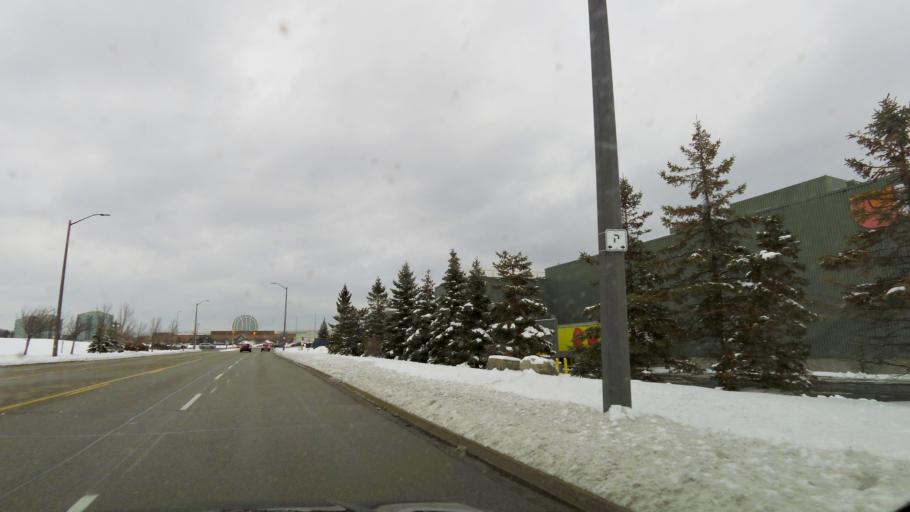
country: CA
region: Ontario
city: Mississauga
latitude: 43.5545
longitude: -79.7162
